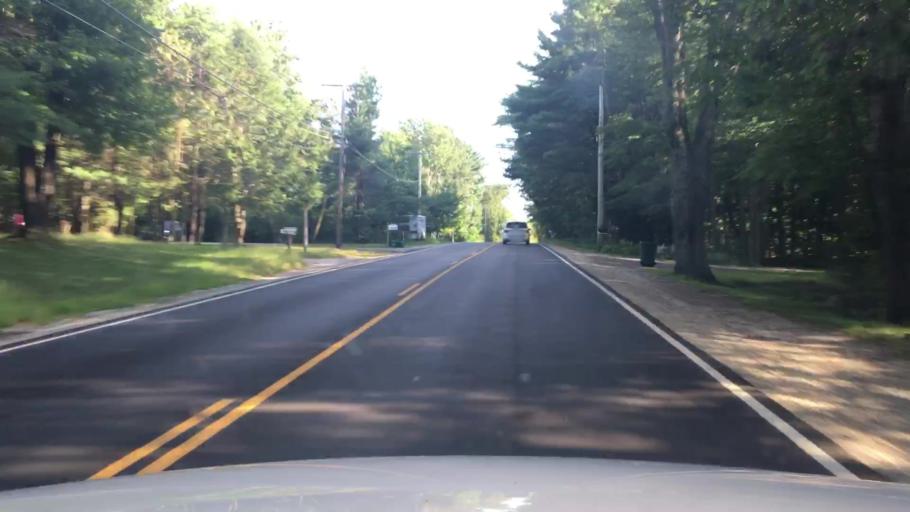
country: US
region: Maine
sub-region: Cumberland County
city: Cumberland Center
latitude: 43.8252
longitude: -70.3166
